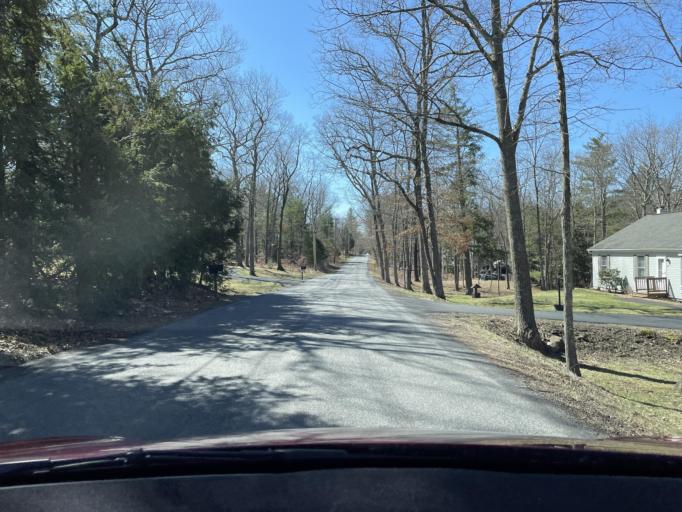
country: US
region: New York
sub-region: Ulster County
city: Manorville
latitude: 42.0723
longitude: -74.0241
